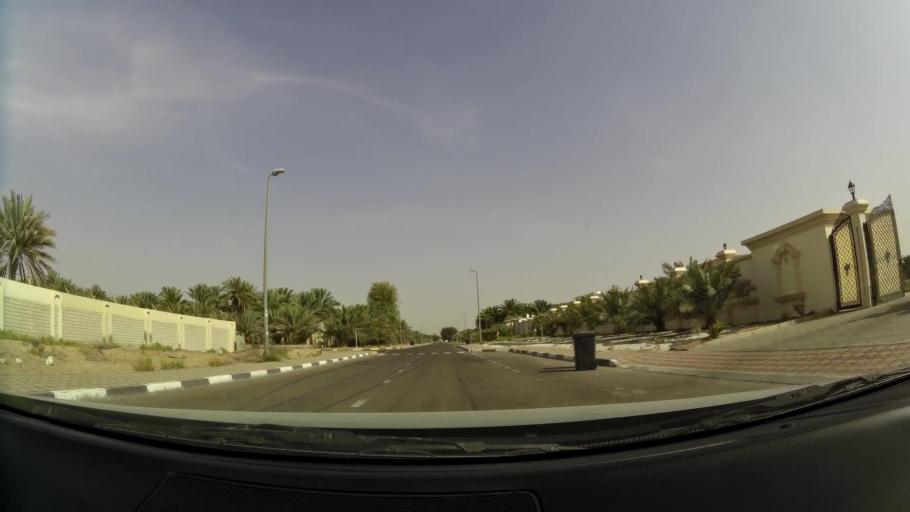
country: AE
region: Abu Dhabi
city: Al Ain
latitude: 24.1590
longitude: 55.7097
